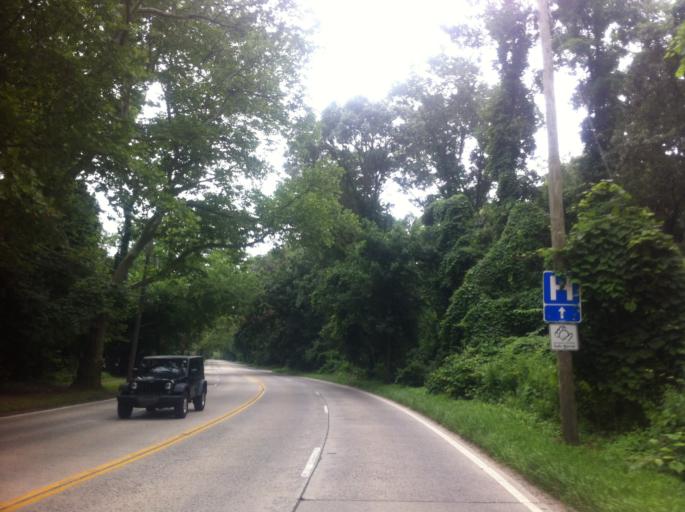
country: US
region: New York
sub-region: Nassau County
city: Lattingtown
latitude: 40.9058
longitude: -73.5847
